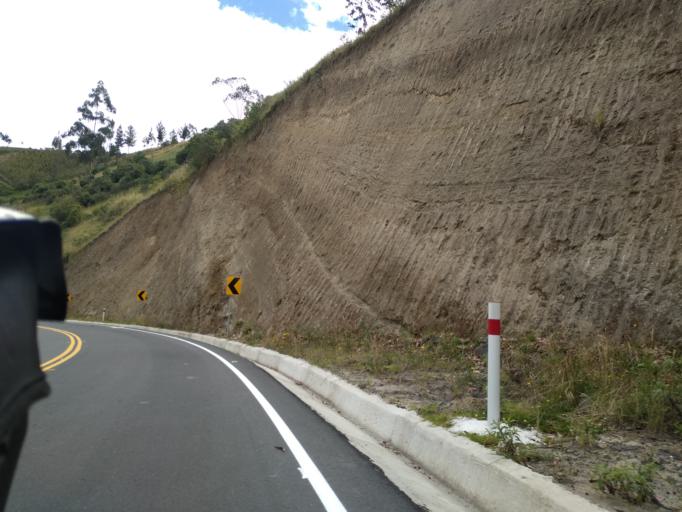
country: EC
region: Cotopaxi
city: Saquisili
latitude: -0.7846
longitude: -78.9120
